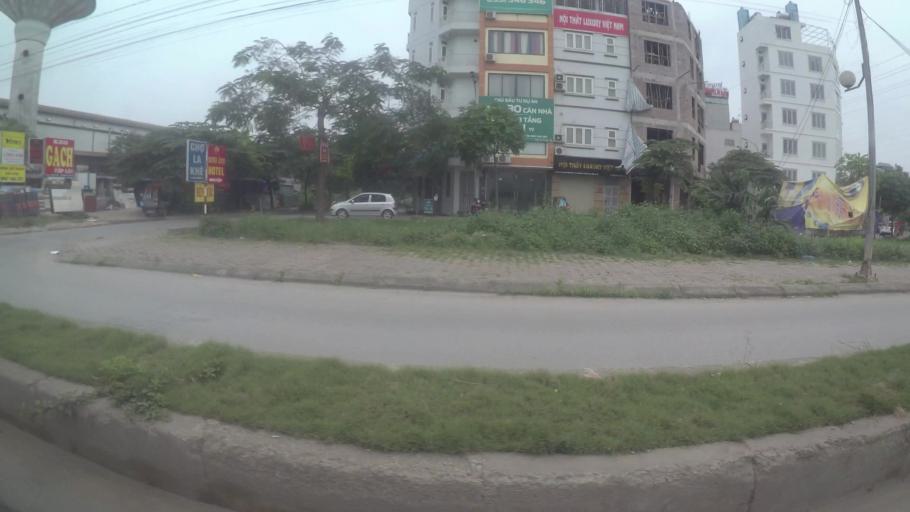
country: VN
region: Ha Noi
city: Ha Dong
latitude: 20.9693
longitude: 105.7528
